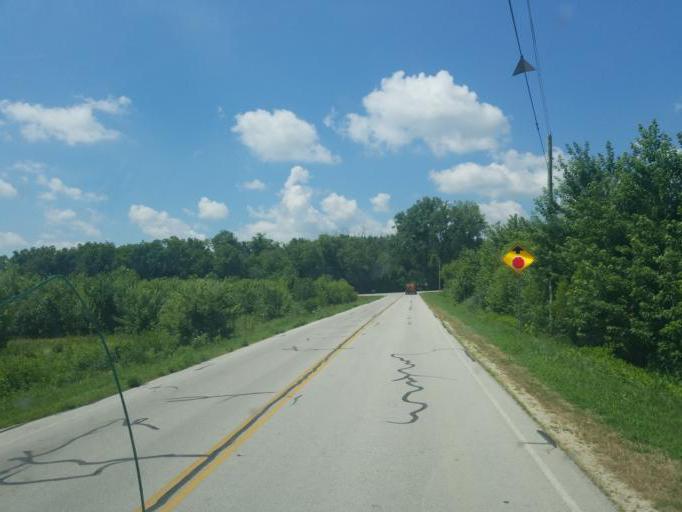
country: US
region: Ohio
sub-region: Mercer County
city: Rockford
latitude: 40.6788
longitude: -84.5170
